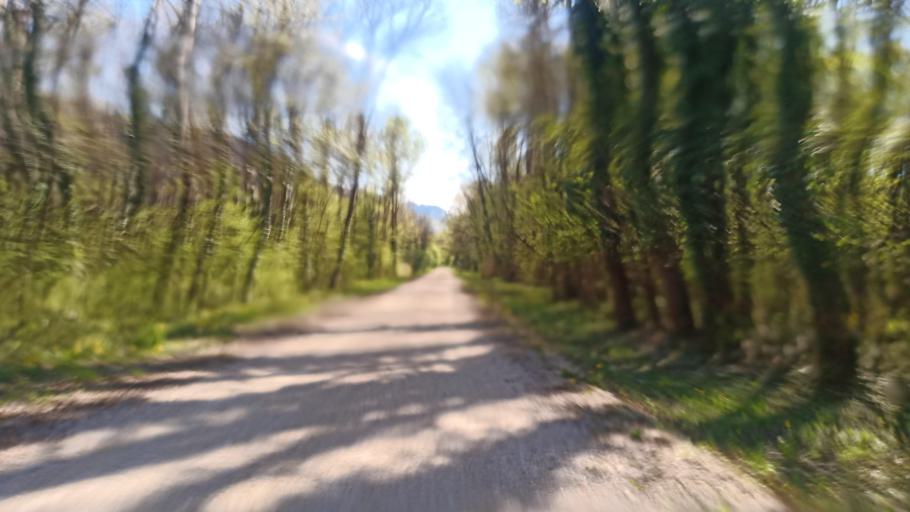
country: FR
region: Rhone-Alpes
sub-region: Departement de l'Isere
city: Froges
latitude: 45.2757
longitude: 5.9158
